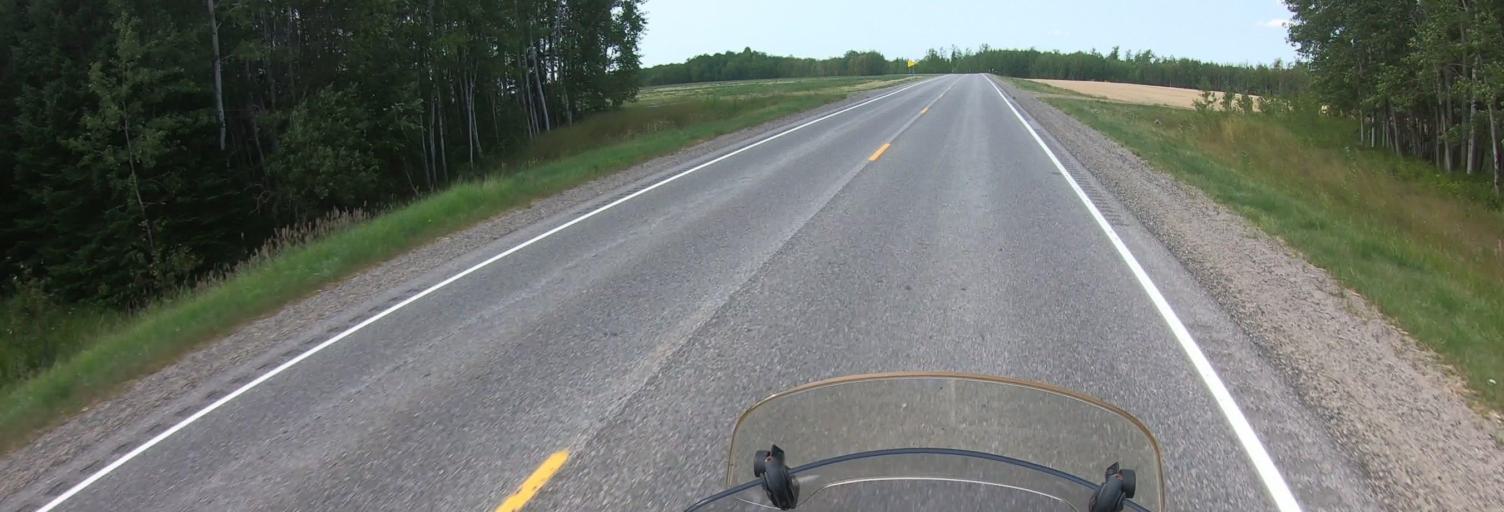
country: US
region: Minnesota
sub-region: Lake of the Woods County
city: Baudette
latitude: 48.6409
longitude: -94.1335
